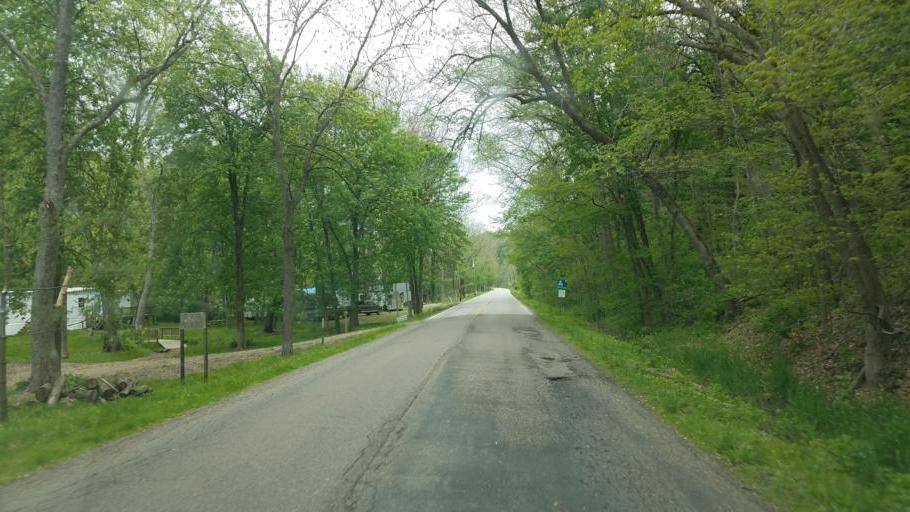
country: US
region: Ohio
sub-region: Ashland County
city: Loudonville
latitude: 40.5947
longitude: -82.2198
